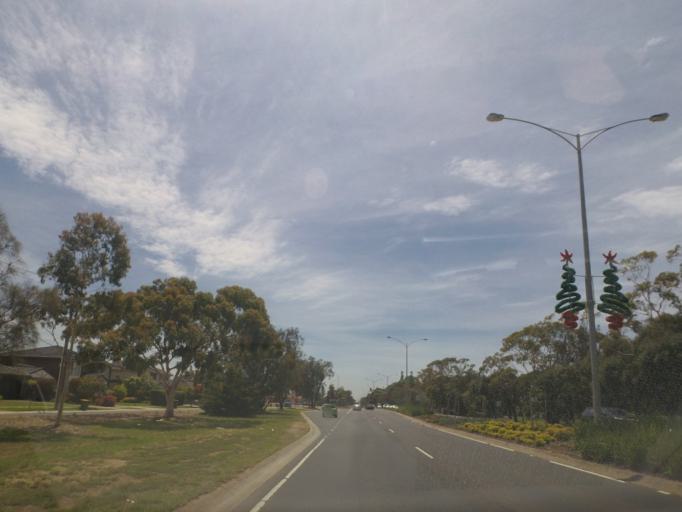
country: AU
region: Victoria
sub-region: Wyndham
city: Werribee
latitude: -37.8945
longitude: 144.6790
